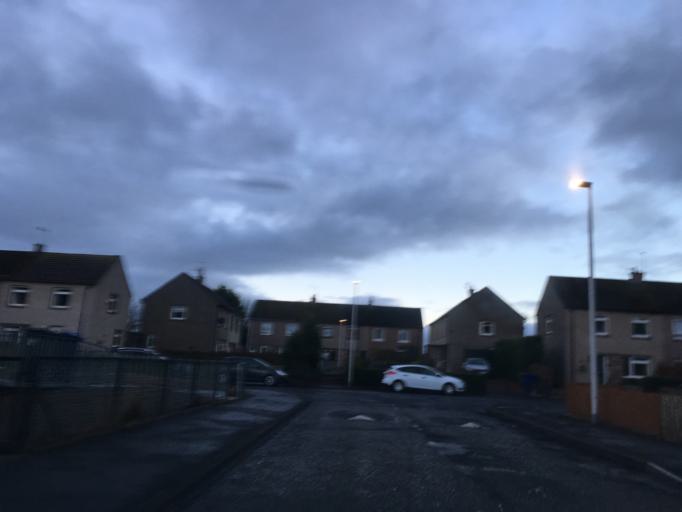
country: GB
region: Scotland
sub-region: Midlothian
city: Loanhead
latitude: 55.8582
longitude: -3.1706
